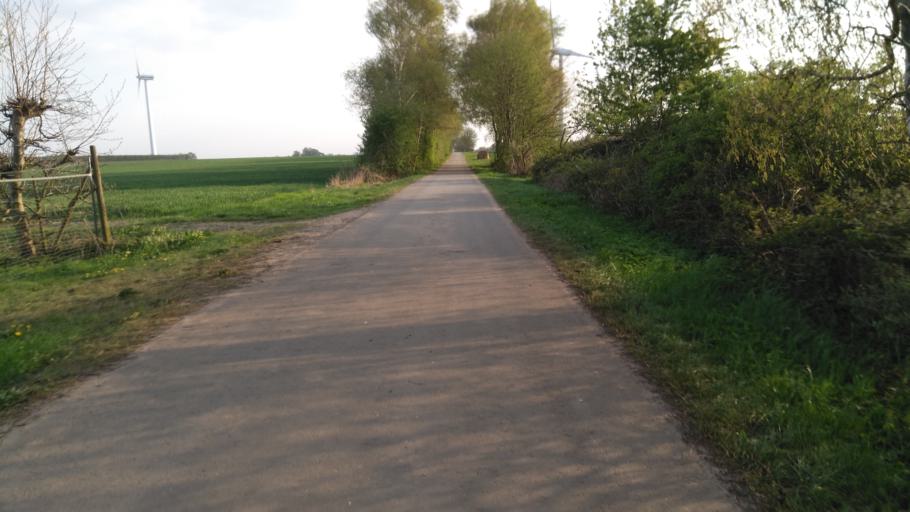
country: DE
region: Lower Saxony
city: Nottensdorf
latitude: 53.4607
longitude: 9.6146
